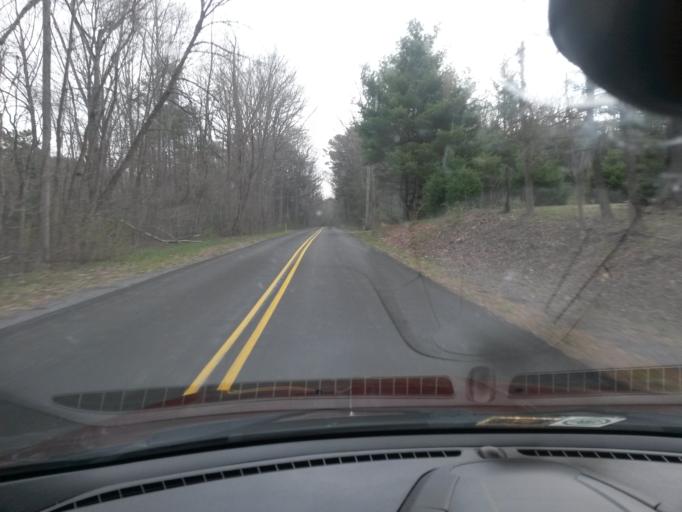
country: US
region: Virginia
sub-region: Alleghany County
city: Clifton Forge
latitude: 37.8177
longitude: -79.6706
